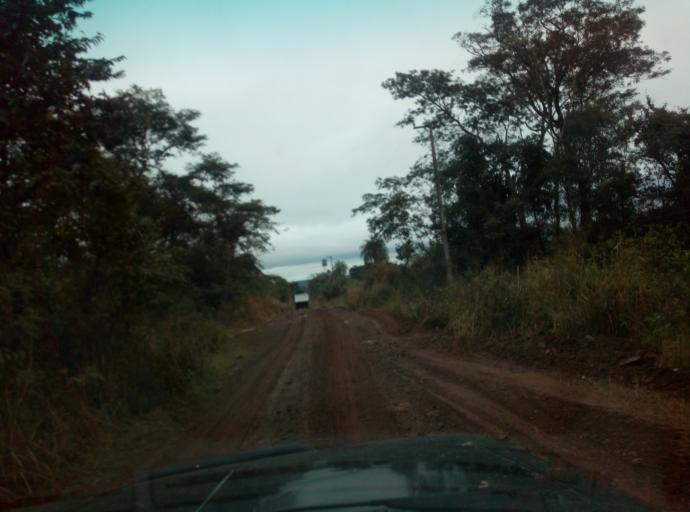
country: PY
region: Caaguazu
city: Carayao
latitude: -25.1902
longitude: -56.3780
